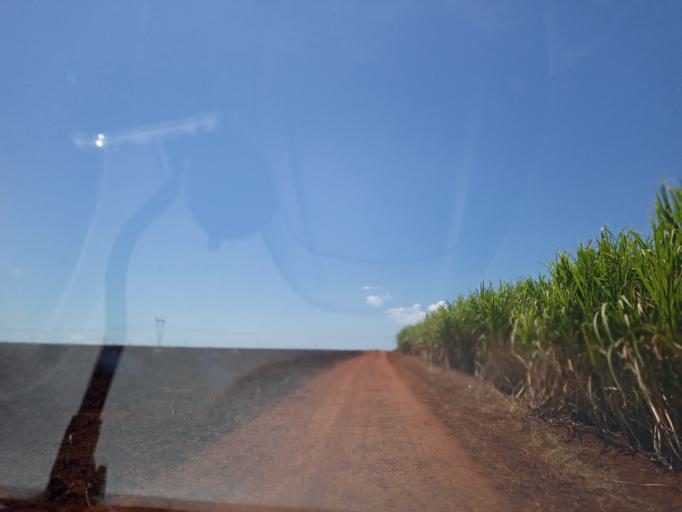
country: BR
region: Goias
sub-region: Itumbiara
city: Itumbiara
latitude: -18.4407
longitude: -49.1359
